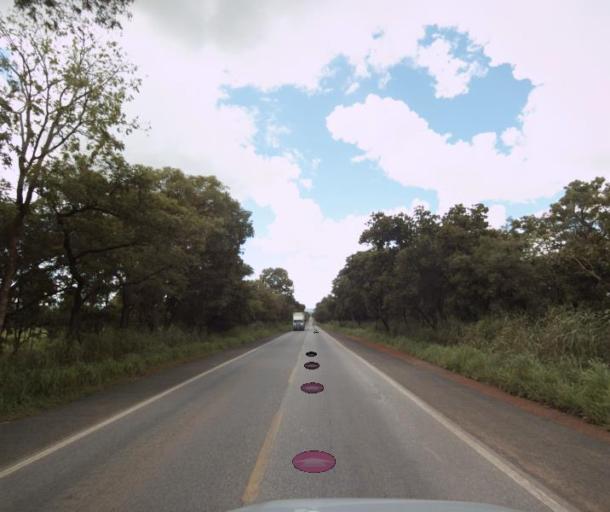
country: BR
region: Goias
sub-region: Porangatu
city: Porangatu
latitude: -13.7922
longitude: -49.0350
